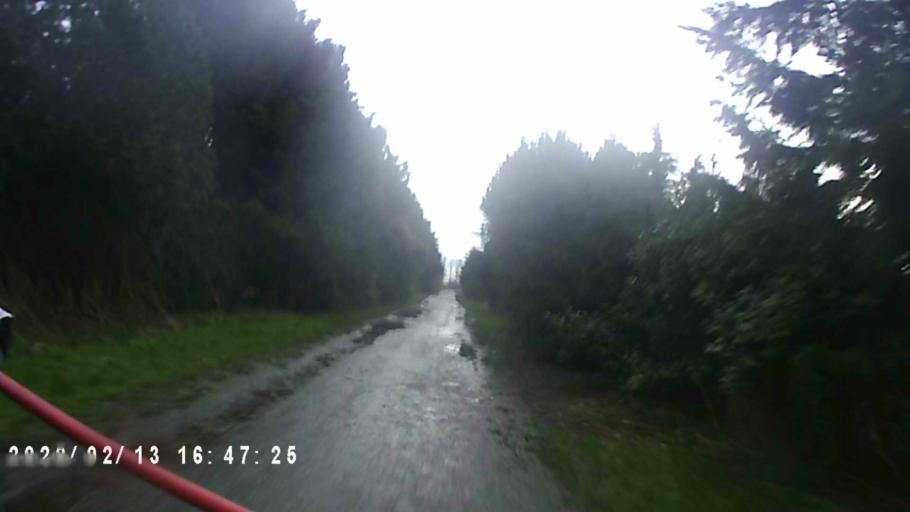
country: NL
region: Groningen
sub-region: Gemeente Groningen
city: Groningen
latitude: 53.2183
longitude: 6.5206
